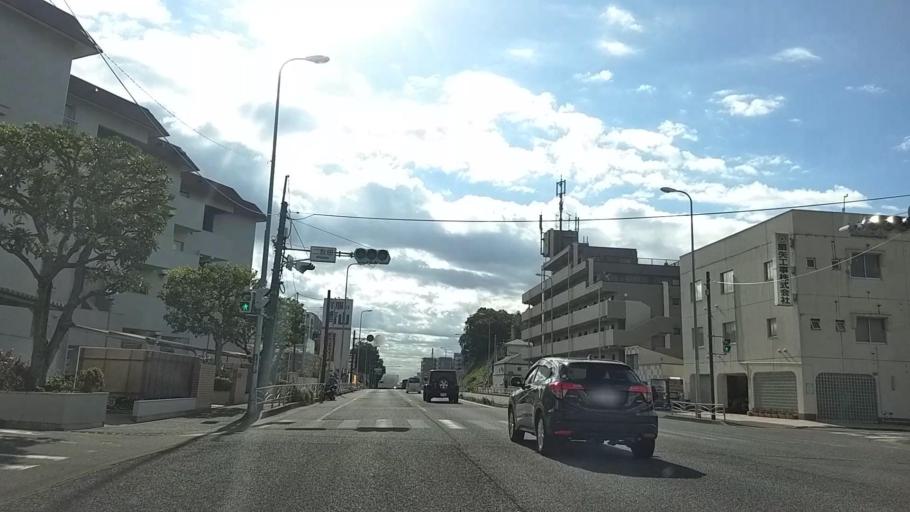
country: JP
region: Kanagawa
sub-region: Kawasaki-shi
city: Kawasaki
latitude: 35.5057
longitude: 139.6620
